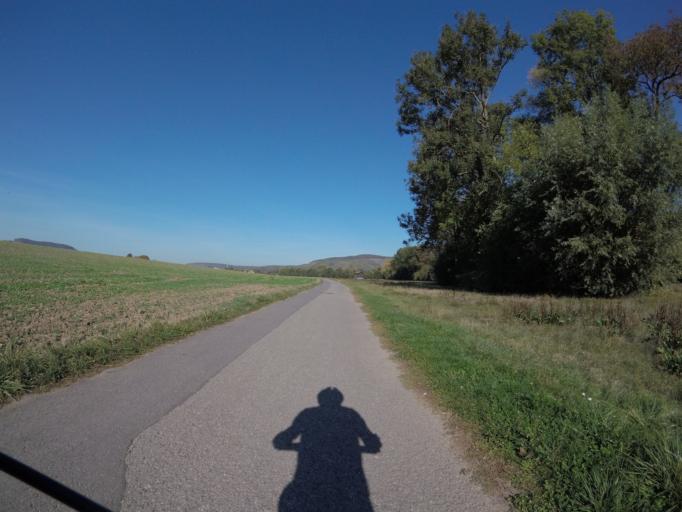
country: DE
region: Baden-Wuerttemberg
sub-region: Regierungsbezirk Stuttgart
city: Sersheim
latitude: 48.9712
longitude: 9.0005
